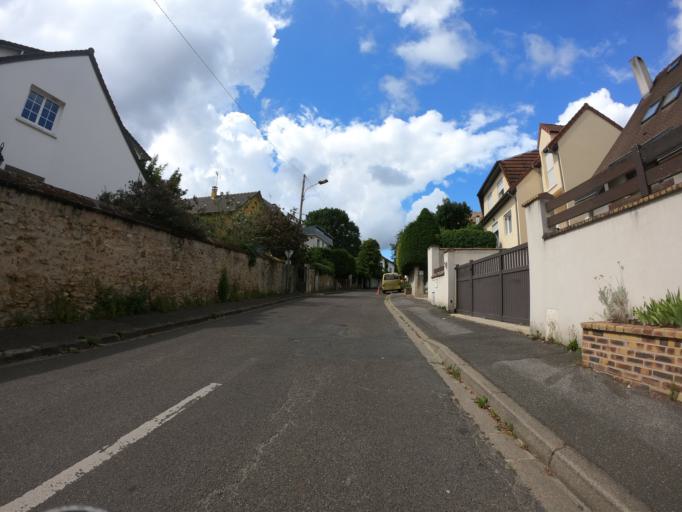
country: FR
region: Ile-de-France
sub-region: Departement de l'Essonne
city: Verrieres-le-Buisson
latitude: 48.7459
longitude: 2.2607
